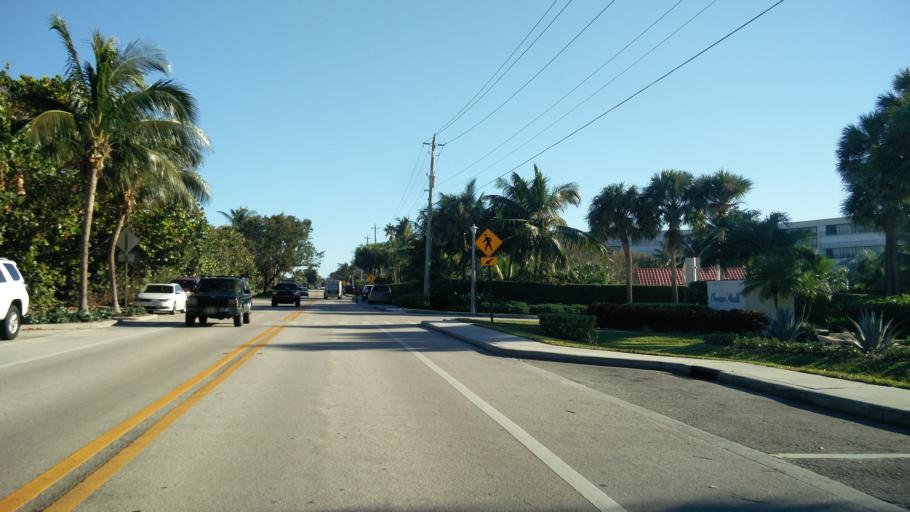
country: US
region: Florida
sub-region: Palm Beach County
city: Jupiter
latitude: 26.9232
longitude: -80.0670
